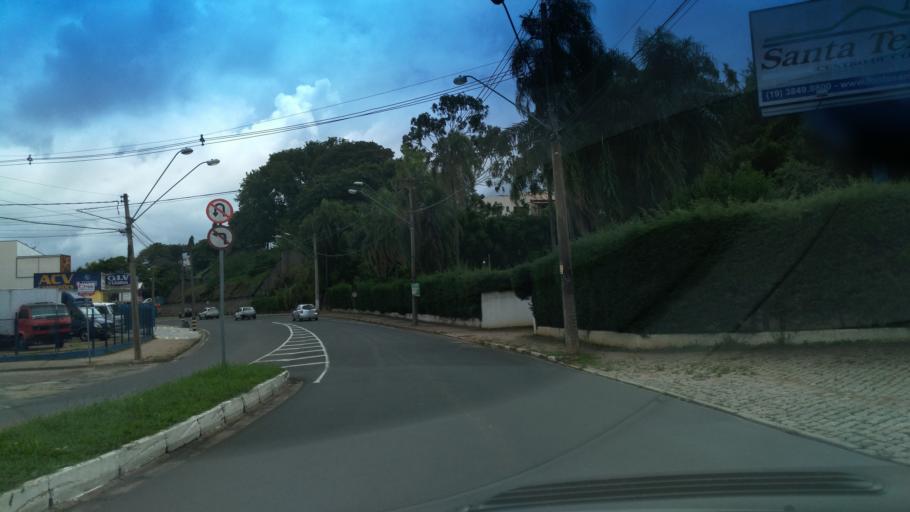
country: BR
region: Sao Paulo
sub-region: Valinhos
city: Valinhos
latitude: -22.9627
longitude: -46.9878
